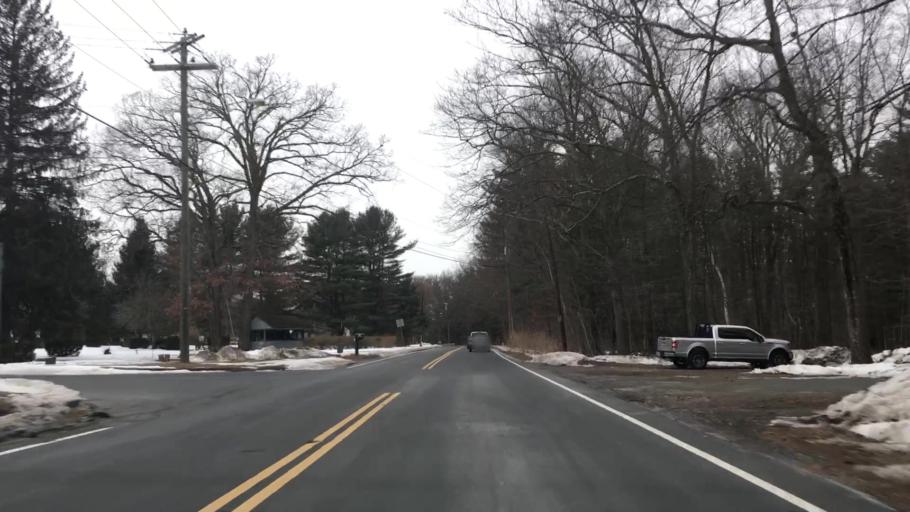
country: US
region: Massachusetts
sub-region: Hampden County
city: Westfield
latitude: 42.1030
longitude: -72.6912
